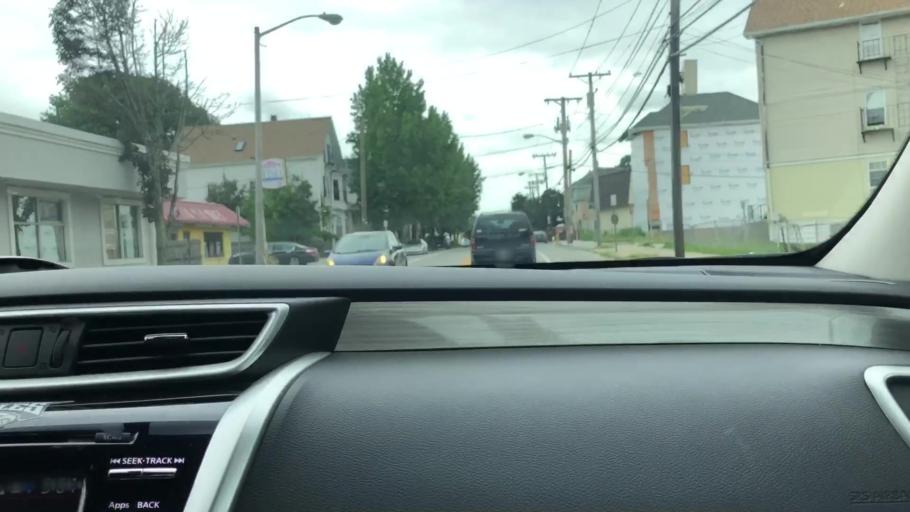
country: US
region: Rhode Island
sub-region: Providence County
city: Central Falls
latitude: 41.8735
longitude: -71.4143
